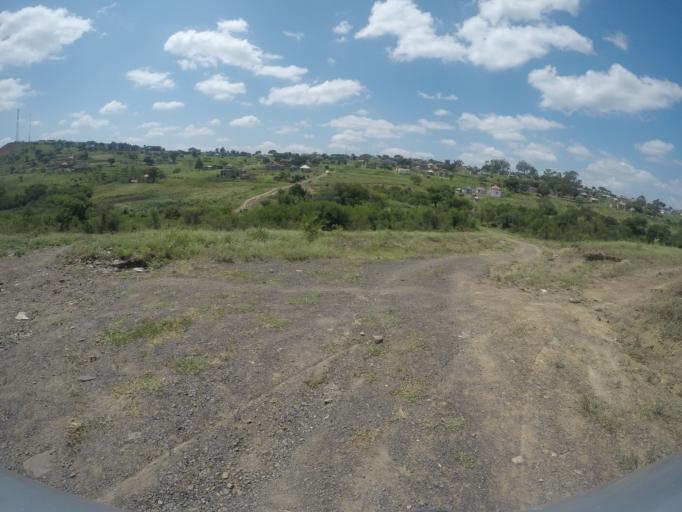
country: ZA
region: KwaZulu-Natal
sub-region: uThungulu District Municipality
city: Empangeni
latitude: -28.6031
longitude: 31.7374
